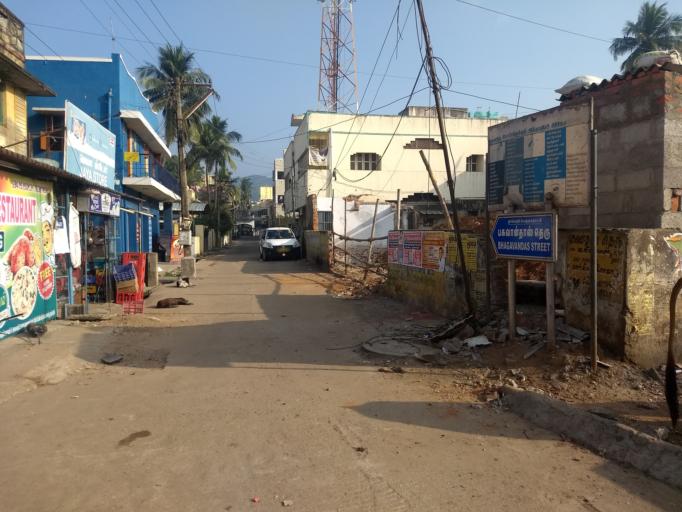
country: IN
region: Tamil Nadu
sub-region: Kancheepuram
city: Vandalur
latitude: 12.9258
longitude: 80.1053
